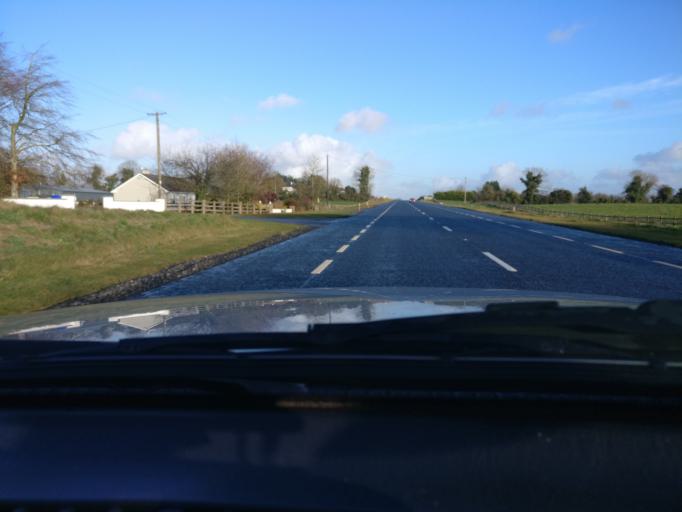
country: IE
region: Leinster
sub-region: An Iarmhi
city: Rathwire
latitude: 53.5549
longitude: -7.2378
